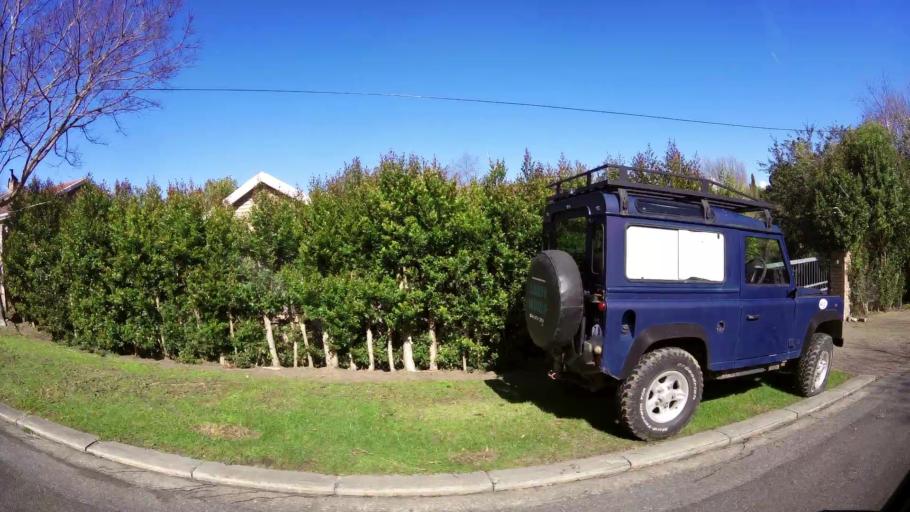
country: ZA
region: Western Cape
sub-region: Eden District Municipality
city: George
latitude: -33.9426
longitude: 22.4702
